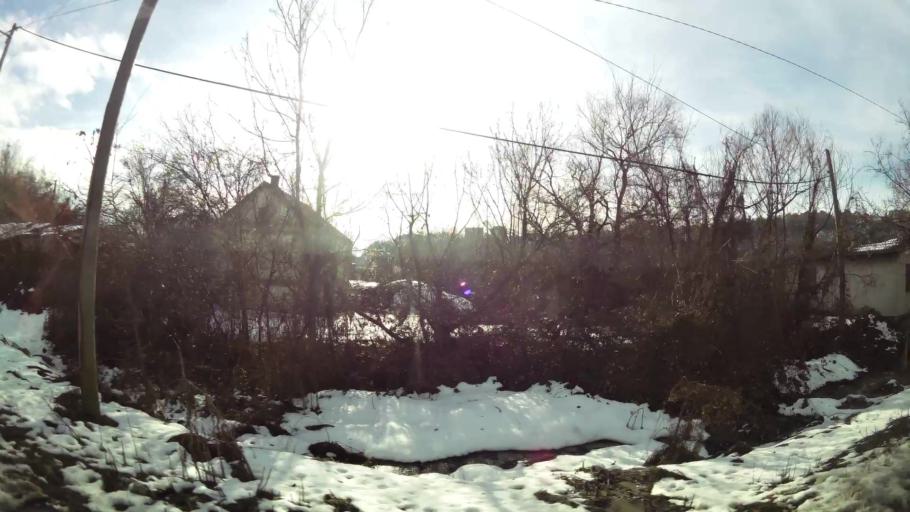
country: RS
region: Central Serbia
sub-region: Belgrade
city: Rakovica
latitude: 44.7260
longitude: 20.4384
